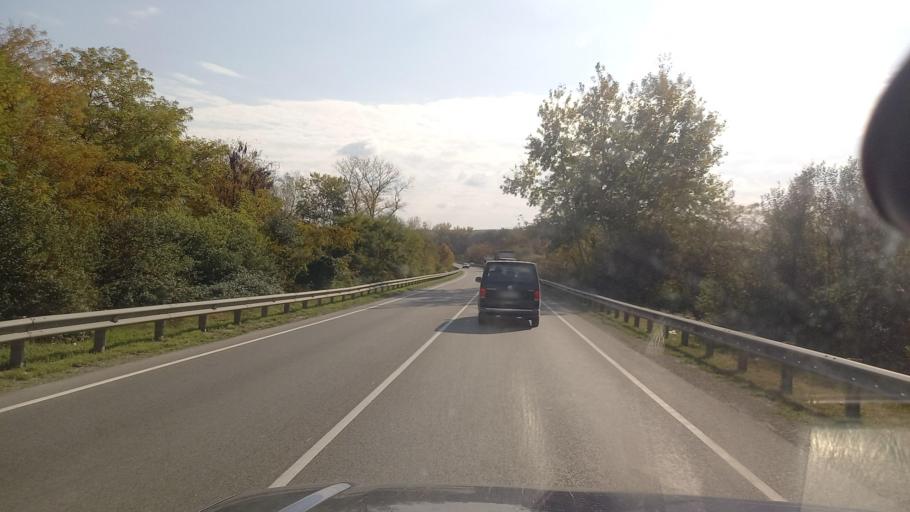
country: RU
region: Krasnodarskiy
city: Abinsk
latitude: 44.8456
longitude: 38.1507
